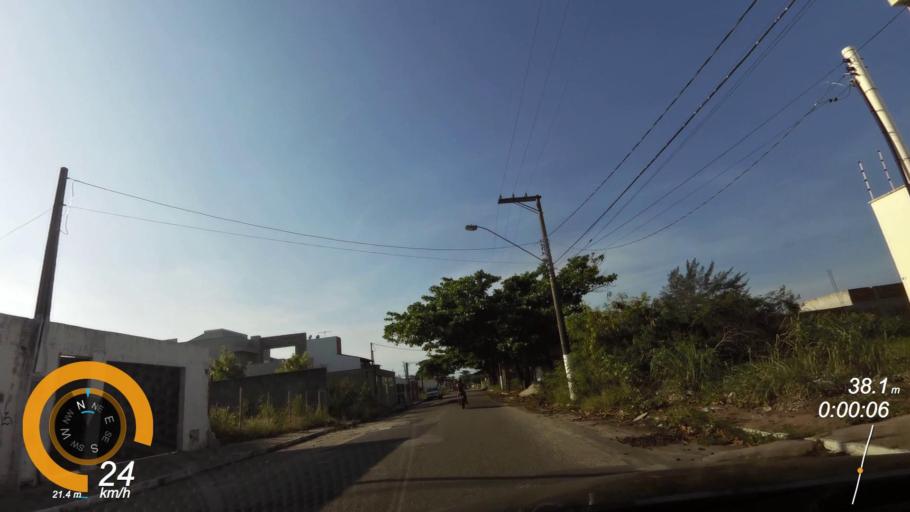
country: BR
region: Espirito Santo
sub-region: Vila Velha
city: Vila Velha
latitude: -20.4859
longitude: -40.3499
